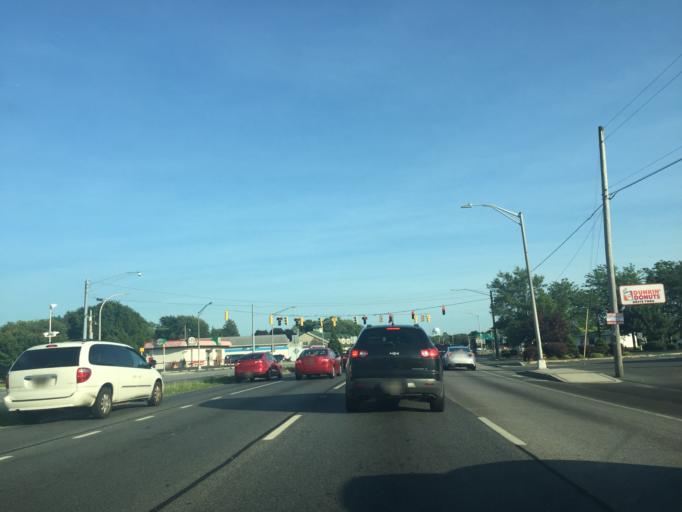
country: US
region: Delaware
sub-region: Kent County
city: Dover
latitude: 39.1689
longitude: -75.5174
